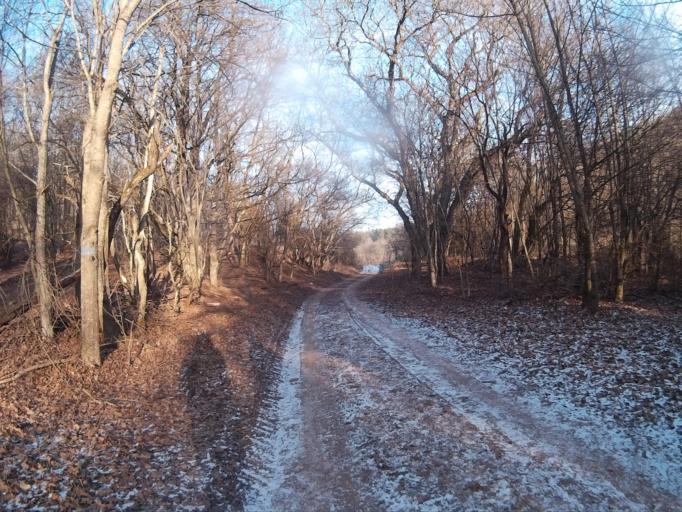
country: SK
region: Kosicky
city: Roznava
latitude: 48.5431
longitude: 20.6444
